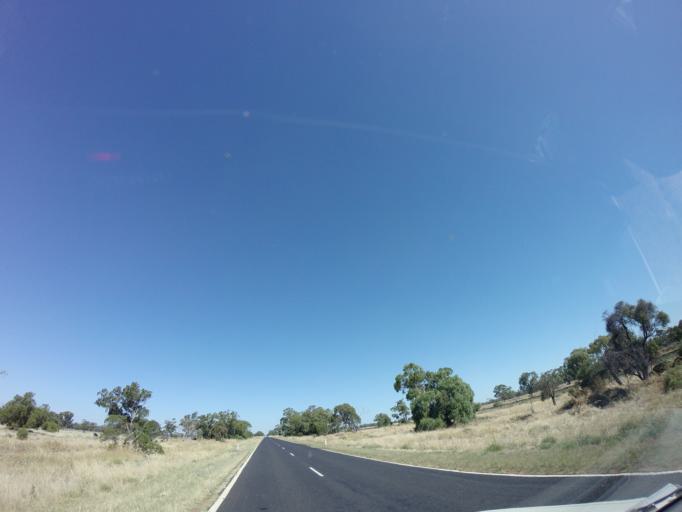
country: AU
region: New South Wales
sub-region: Bogan
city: Nyngan
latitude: -31.7652
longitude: 147.5799
